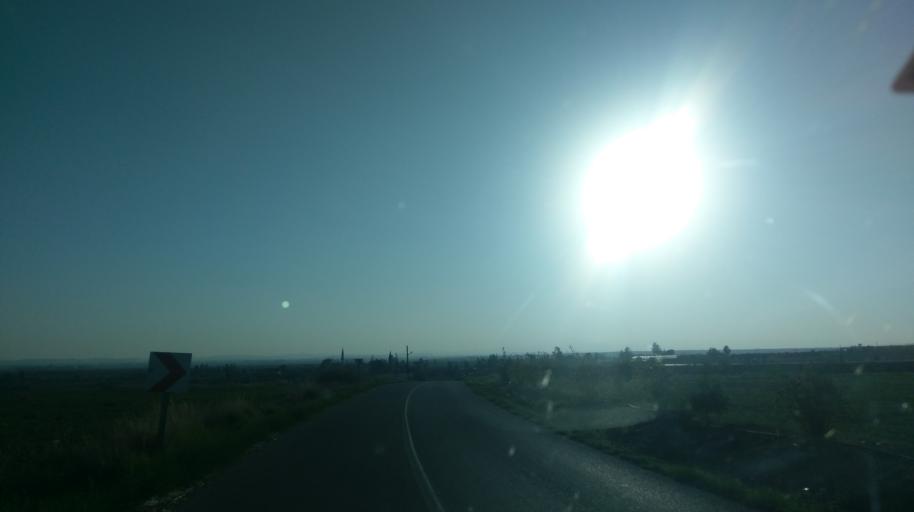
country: CY
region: Ammochostos
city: Lefkonoiko
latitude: 35.2500
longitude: 33.6512
